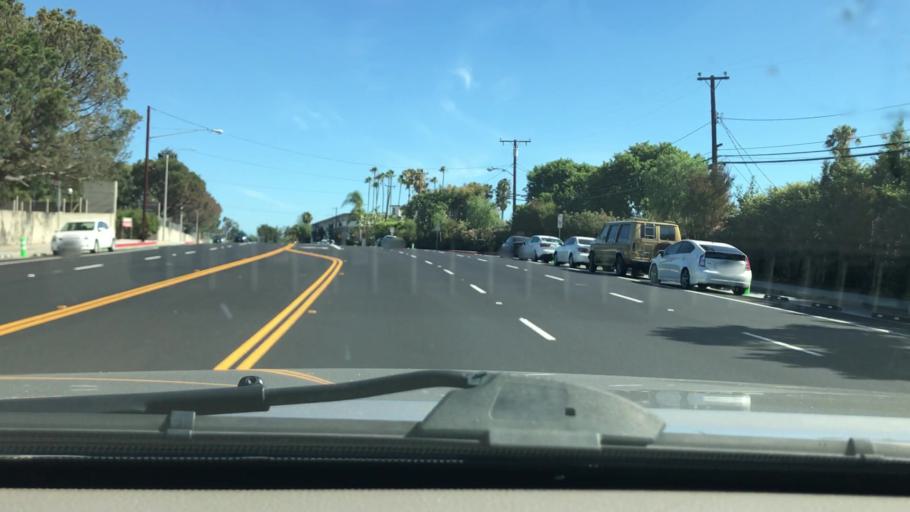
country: US
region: California
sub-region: Orange County
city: Rossmoor
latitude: 33.7787
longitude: -118.1224
